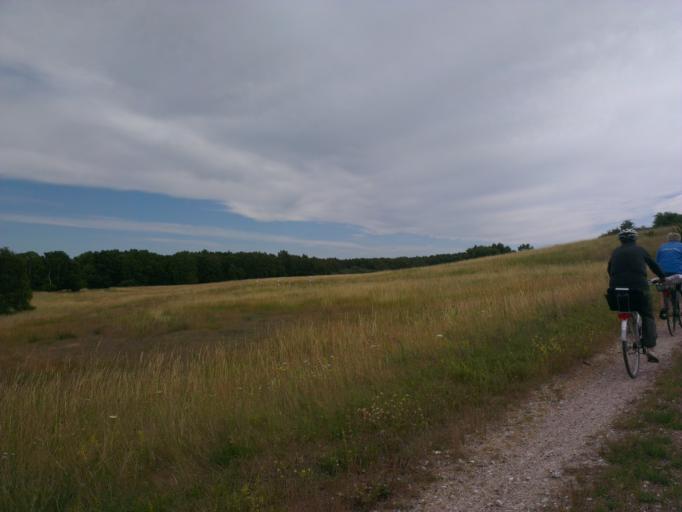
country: DK
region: Capital Region
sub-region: Frederikssund Kommune
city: Jaegerspris
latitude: 55.8990
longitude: 11.9395
